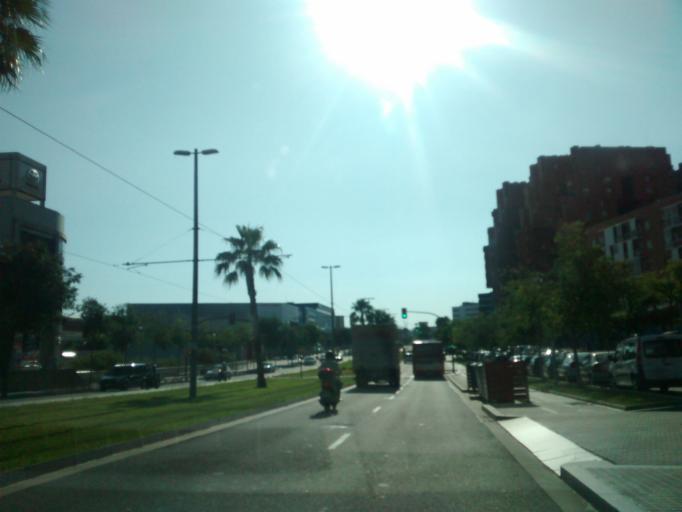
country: ES
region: Catalonia
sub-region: Provincia de Barcelona
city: Sant Just Desvern
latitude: 41.3795
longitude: 2.0700
